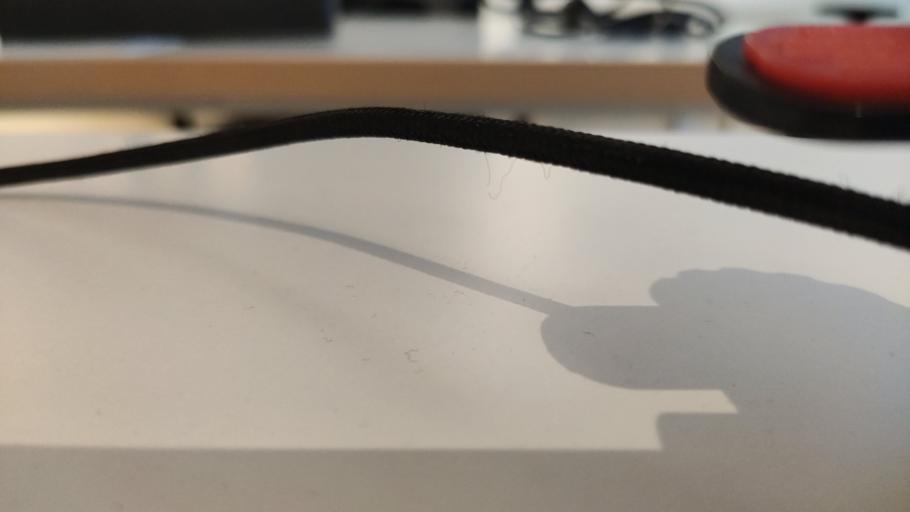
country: RU
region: Moskovskaya
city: Ruza
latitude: 55.8065
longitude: 36.2930
